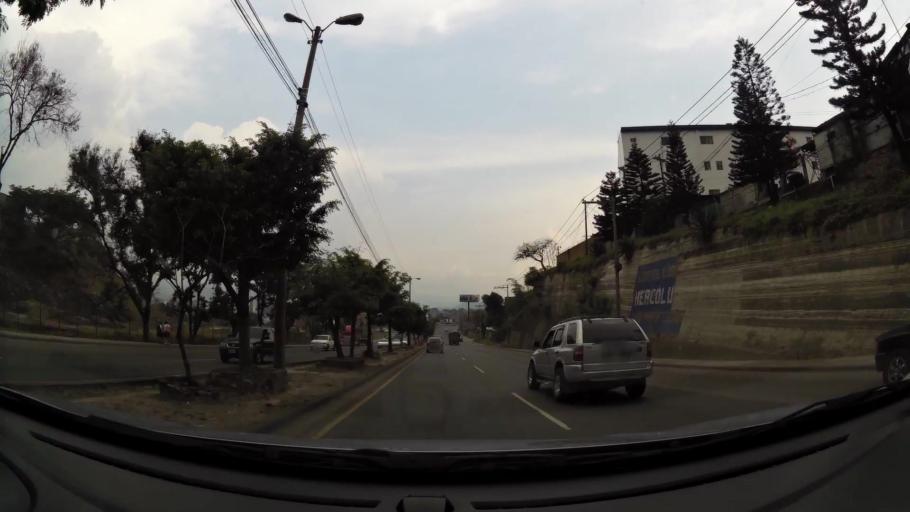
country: HN
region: Francisco Morazan
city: Tegucigalpa
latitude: 14.0774
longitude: -87.2154
